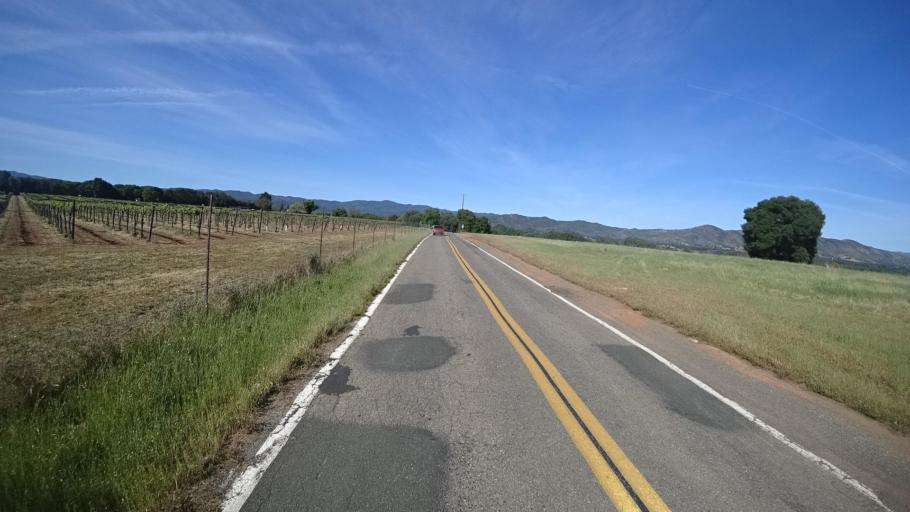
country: US
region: California
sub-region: Lake County
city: Kelseyville
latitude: 38.9666
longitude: -122.8718
